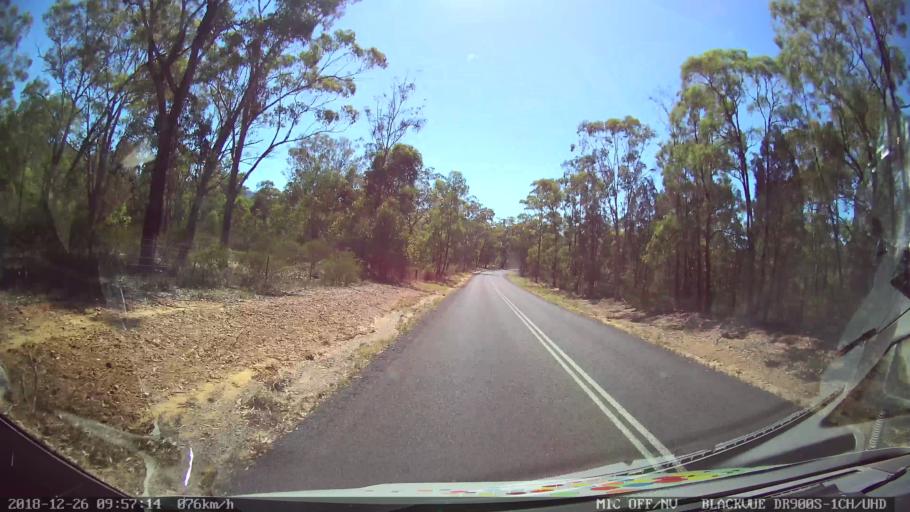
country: AU
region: New South Wales
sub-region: Mid-Western Regional
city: Kandos
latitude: -33.0397
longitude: 150.1897
